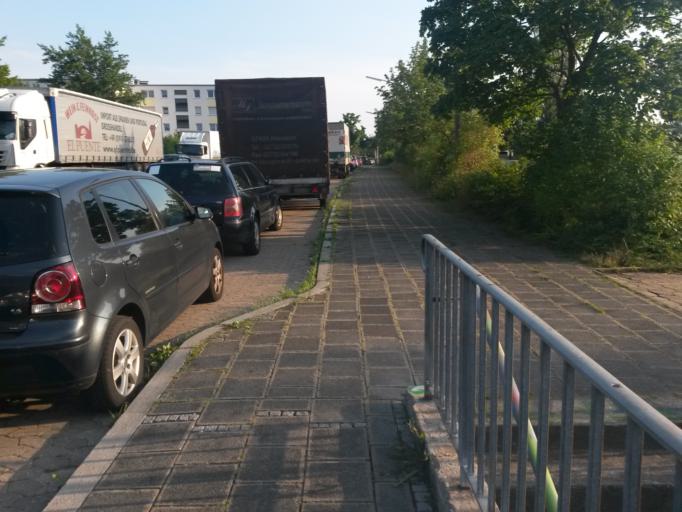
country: DE
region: Bavaria
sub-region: Regierungsbezirk Mittelfranken
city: Oberasbach
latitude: 49.4327
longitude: 10.9619
